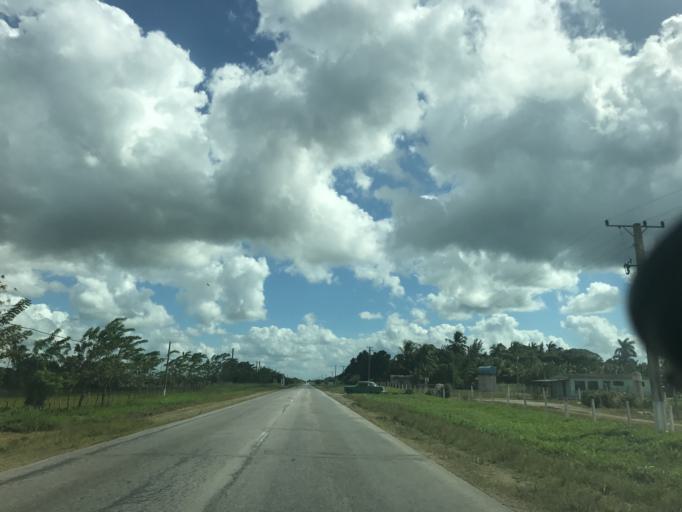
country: CU
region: Camaguey
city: Florida
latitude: 21.4781
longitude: -78.1775
